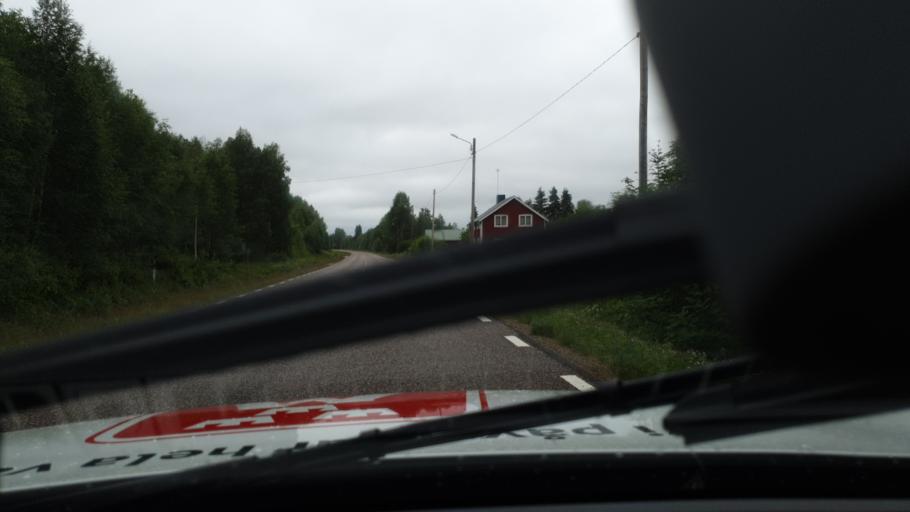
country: FI
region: Lapland
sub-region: Torniolaakso
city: Pello
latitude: 66.9448
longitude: 23.8507
